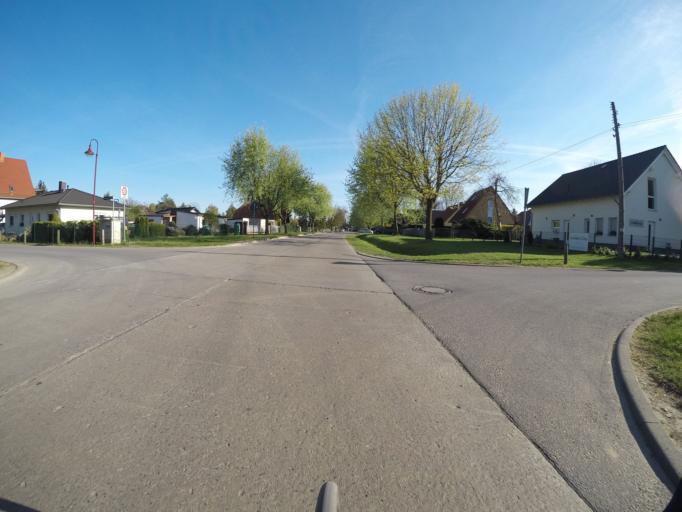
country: DE
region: Brandenburg
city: Neuenhagen
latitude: 52.5149
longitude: 13.7231
